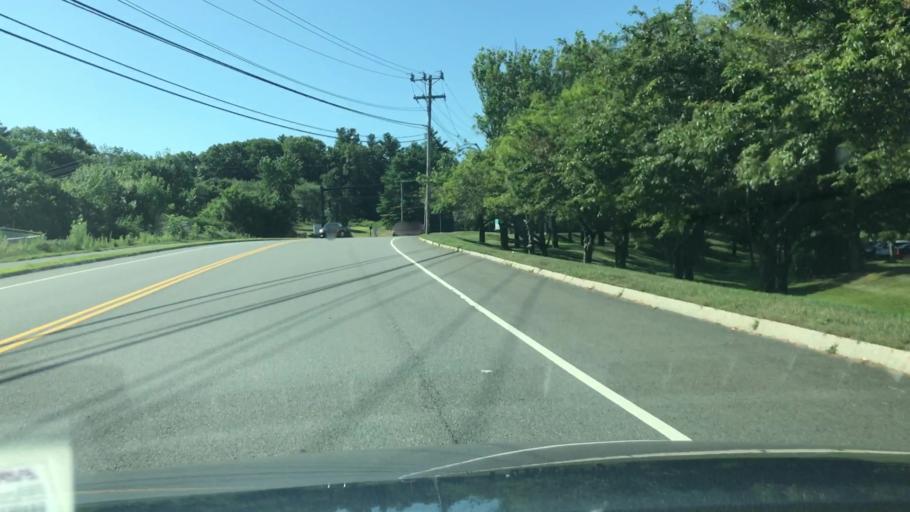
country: US
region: Massachusetts
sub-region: Middlesex County
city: Marlborough
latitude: 42.3326
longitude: -71.5865
